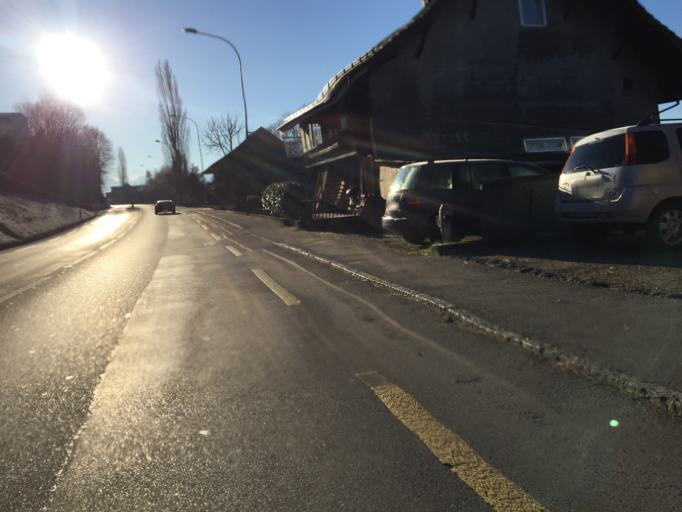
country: CH
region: Bern
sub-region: Bern-Mittelland District
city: Munsingen
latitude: 46.8820
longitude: 7.5580
